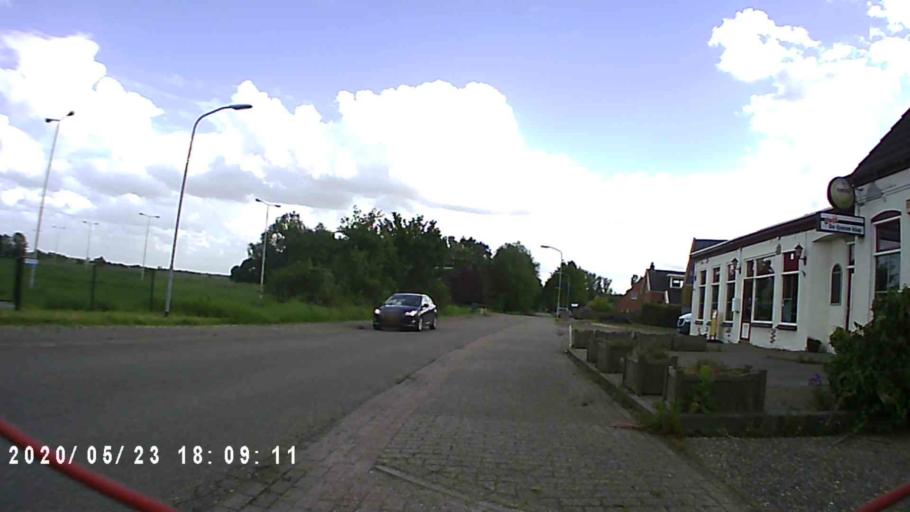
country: NL
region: Groningen
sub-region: Gemeente Hoogezand-Sappemeer
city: Hoogezand
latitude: 53.2349
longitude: 6.7116
